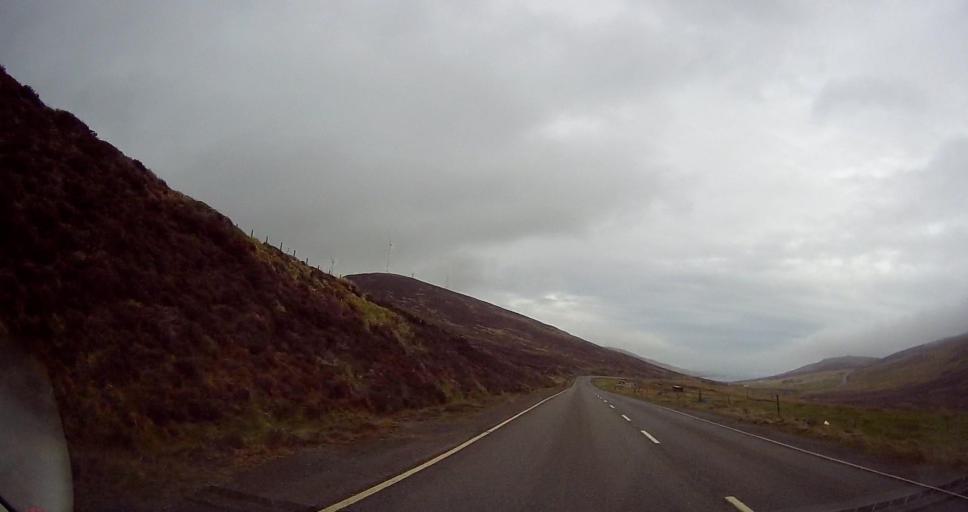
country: GB
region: Scotland
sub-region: Shetland Islands
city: Lerwick
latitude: 60.1533
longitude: -1.2358
